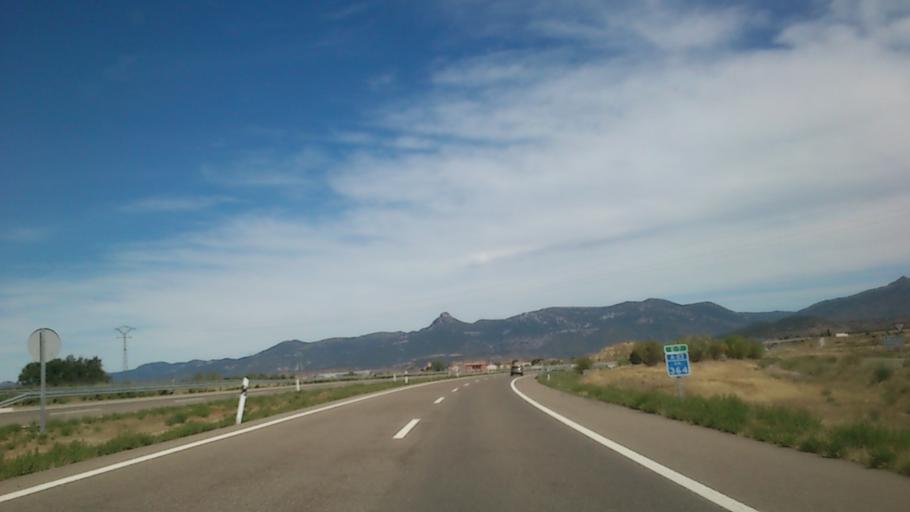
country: ES
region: Aragon
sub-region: Provincia de Huesca
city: Chimillas
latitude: 42.1731
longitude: -0.4311
